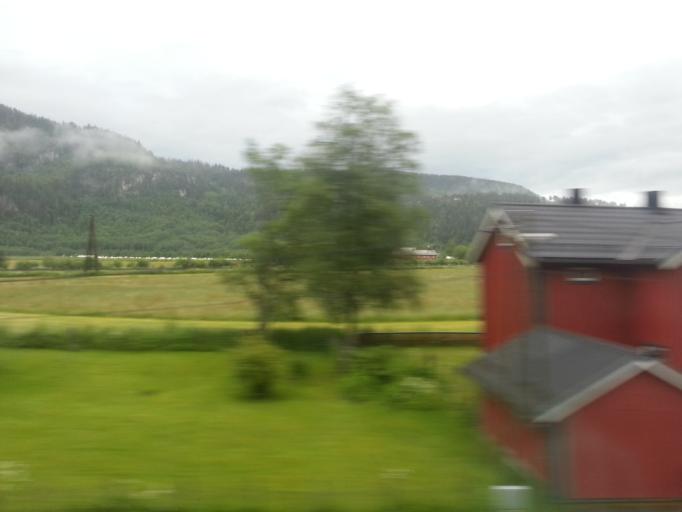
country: NO
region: Sor-Trondelag
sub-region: Midtre Gauldal
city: Storen
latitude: 63.0470
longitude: 10.2835
